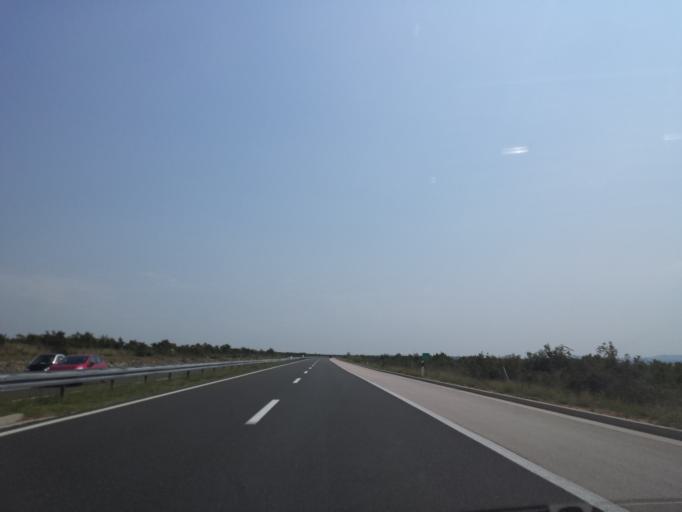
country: HR
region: Zadarska
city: Polaca
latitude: 44.0413
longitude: 15.5530
